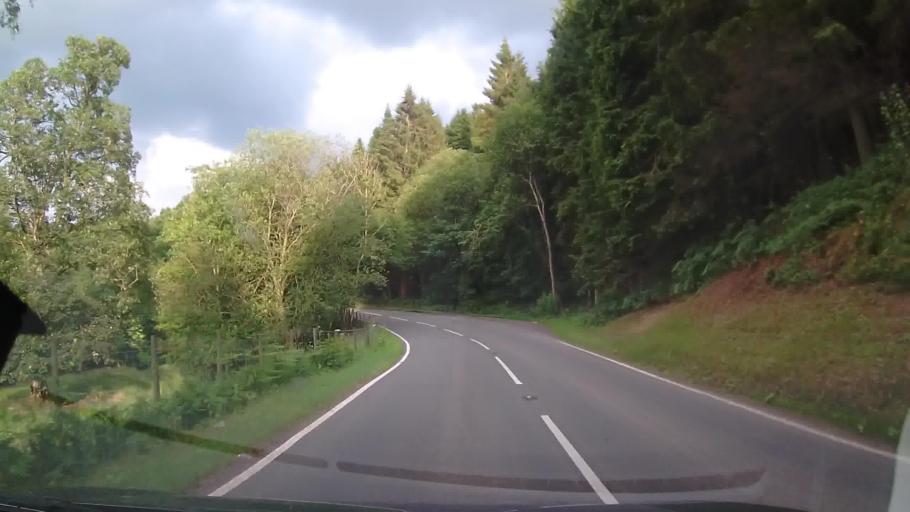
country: GB
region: Wales
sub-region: Gwynedd
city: Bala
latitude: 52.9053
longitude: -3.5292
